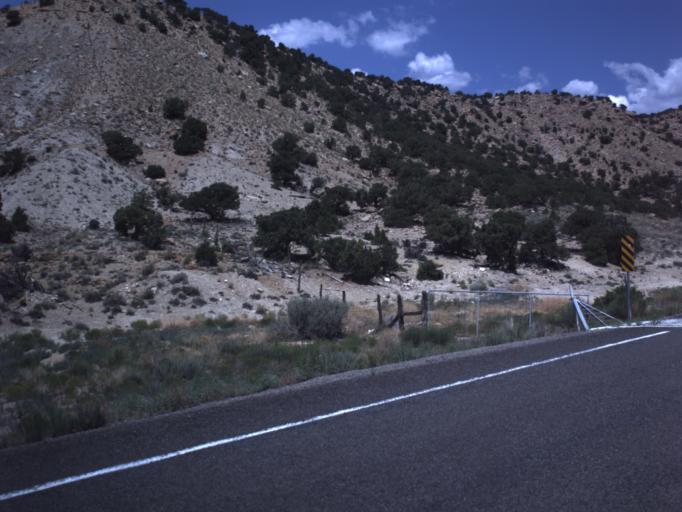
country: US
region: Utah
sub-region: Emery County
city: Orangeville
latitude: 39.2696
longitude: -111.1019
